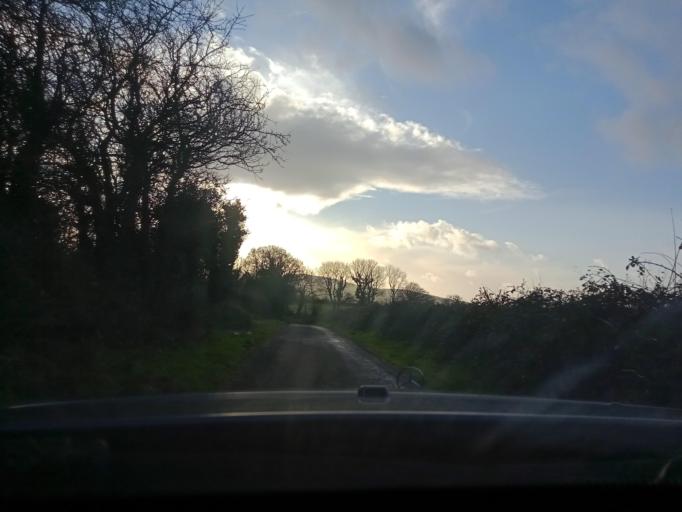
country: IE
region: Leinster
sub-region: Kilkenny
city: Callan
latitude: 52.4535
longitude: -7.4205
